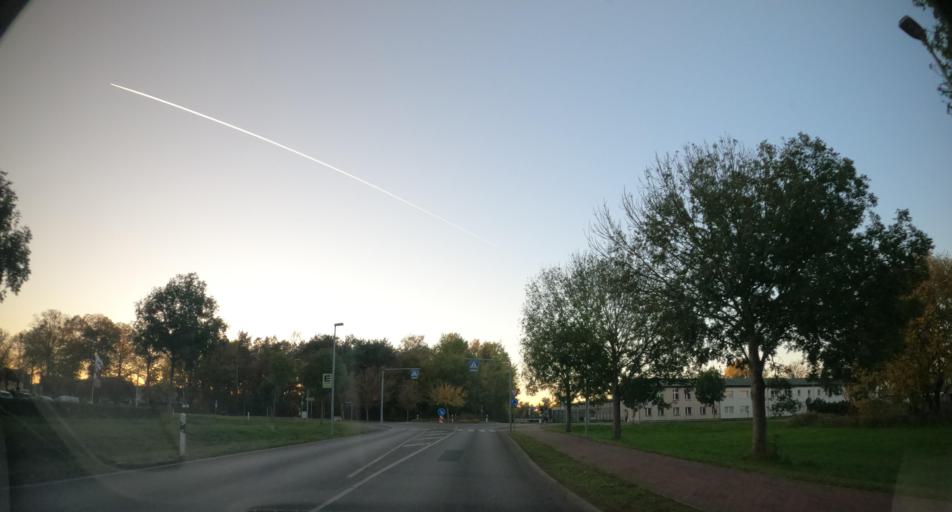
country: DE
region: Mecklenburg-Vorpommern
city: Ueckermunde
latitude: 53.7310
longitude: 14.0359
